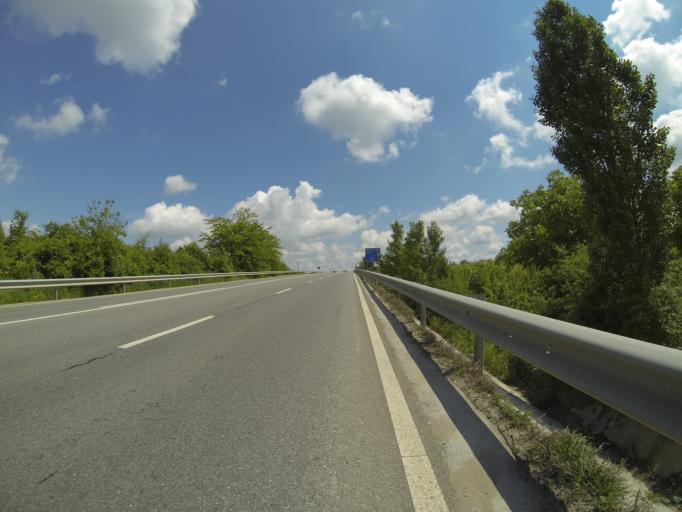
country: RO
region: Dolj
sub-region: Comuna Carcea
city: Carcea
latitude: 44.2652
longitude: 23.8953
